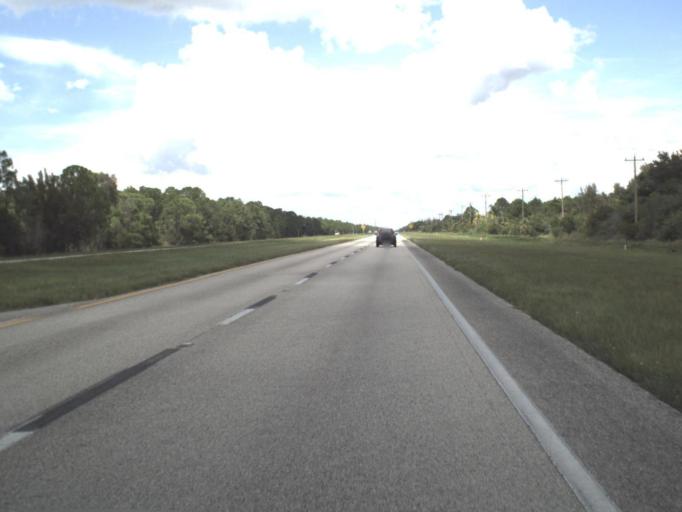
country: US
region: Florida
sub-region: Lee County
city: Burnt Store Marina
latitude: 26.7946
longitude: -81.9469
